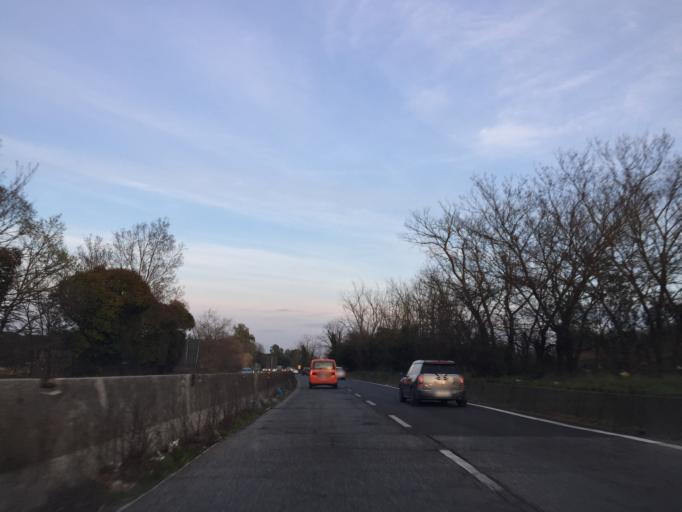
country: IT
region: Latium
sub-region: Citta metropolitana di Roma Capitale
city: Formello
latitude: 42.0448
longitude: 12.3986
